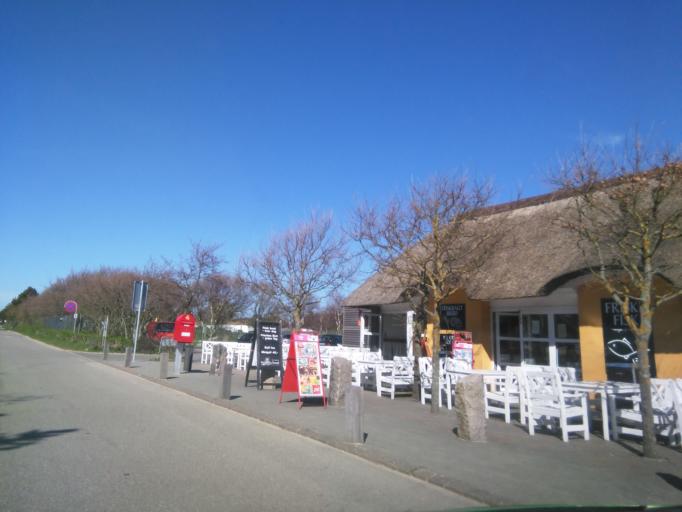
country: DK
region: South Denmark
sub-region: Varde Kommune
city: Oksbol
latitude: 55.5462
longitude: 8.1339
